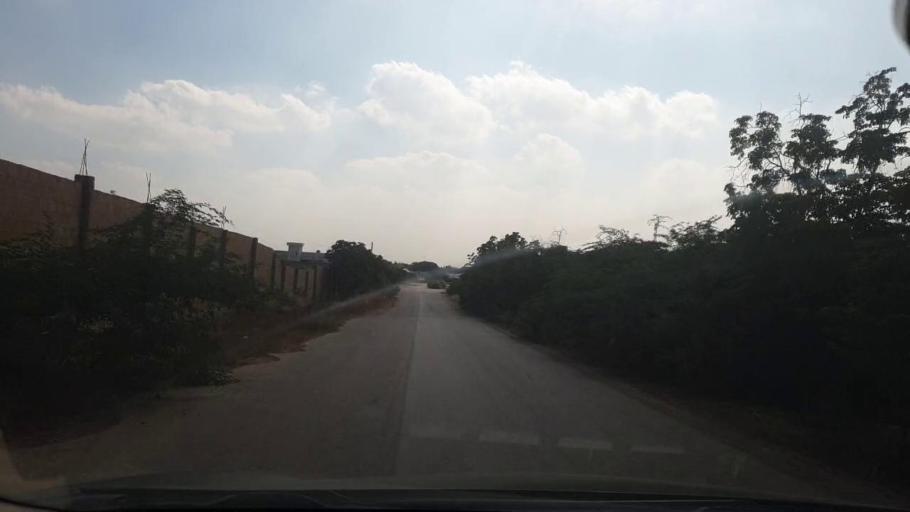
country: PK
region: Sindh
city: Malir Cantonment
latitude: 25.0092
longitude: 67.3554
